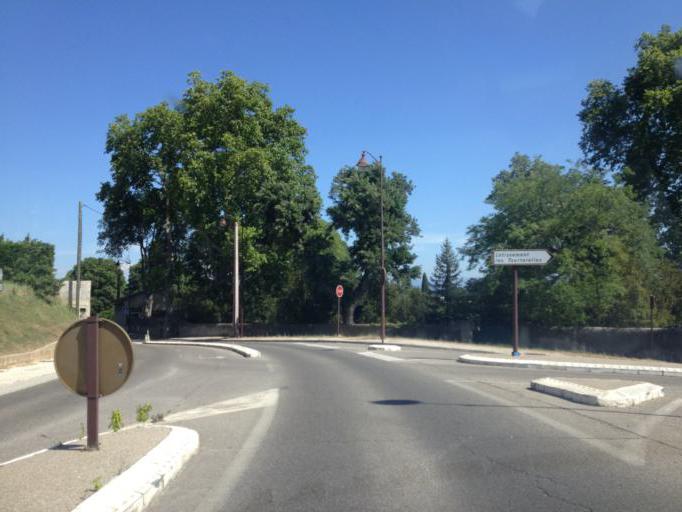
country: FR
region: Provence-Alpes-Cote d'Azur
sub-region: Departement du Vaucluse
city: Cadenet
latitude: 43.7353
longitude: 5.3609
